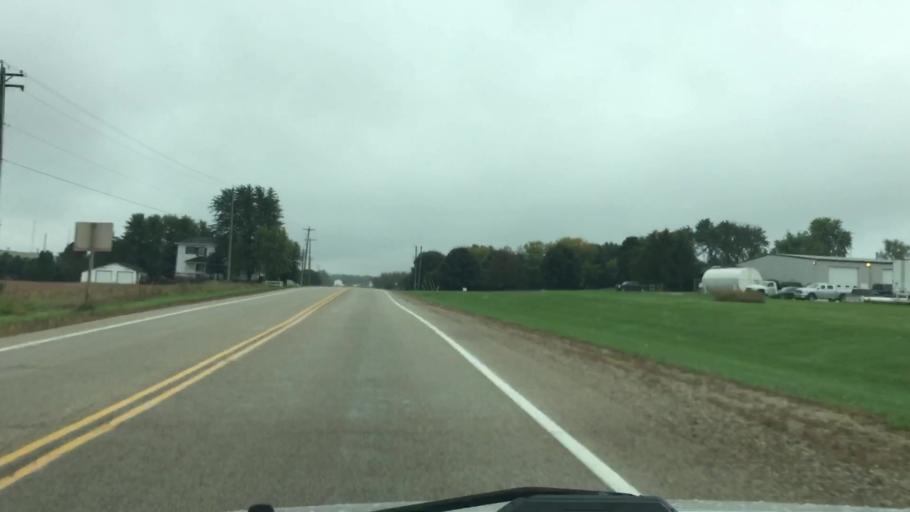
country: US
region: Wisconsin
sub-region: Walworth County
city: Whitewater
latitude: 42.8528
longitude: -88.7188
